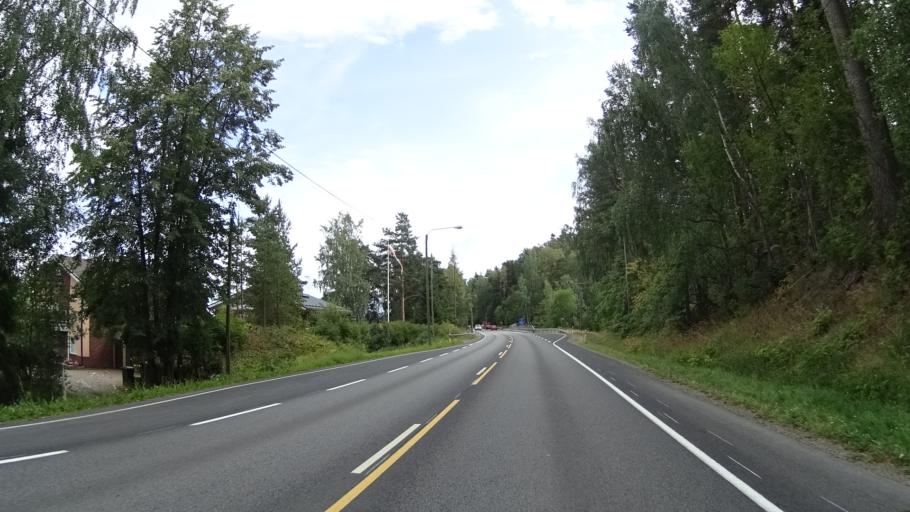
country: FI
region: Pirkanmaa
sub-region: Tampere
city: Kangasala
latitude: 61.4215
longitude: 24.1406
